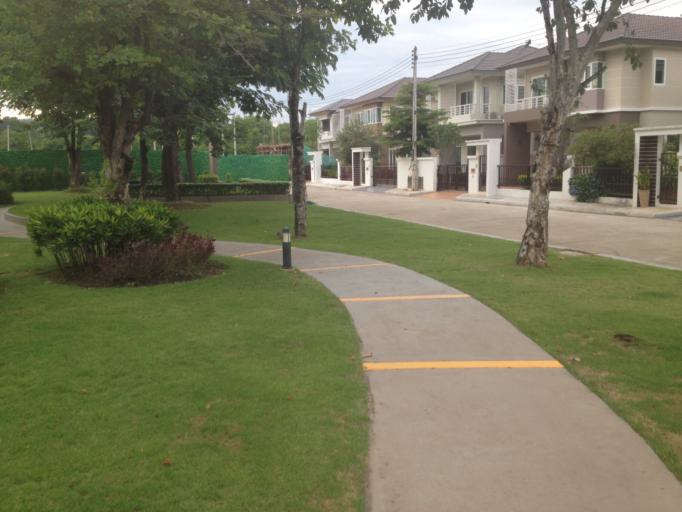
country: TH
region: Chiang Mai
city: Hang Dong
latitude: 18.7067
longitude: 98.9072
